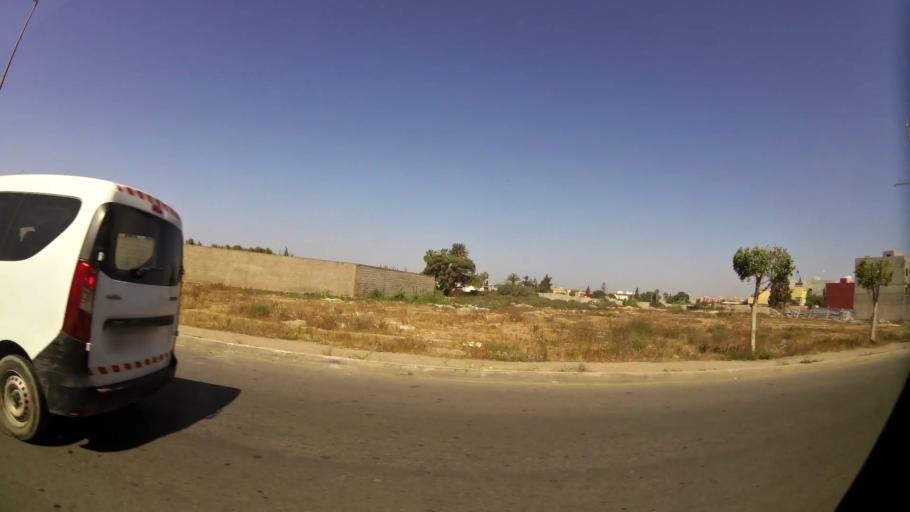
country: MA
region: Souss-Massa-Draa
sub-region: Inezgane-Ait Mellou
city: Inezgane
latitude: 30.3436
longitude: -9.5079
